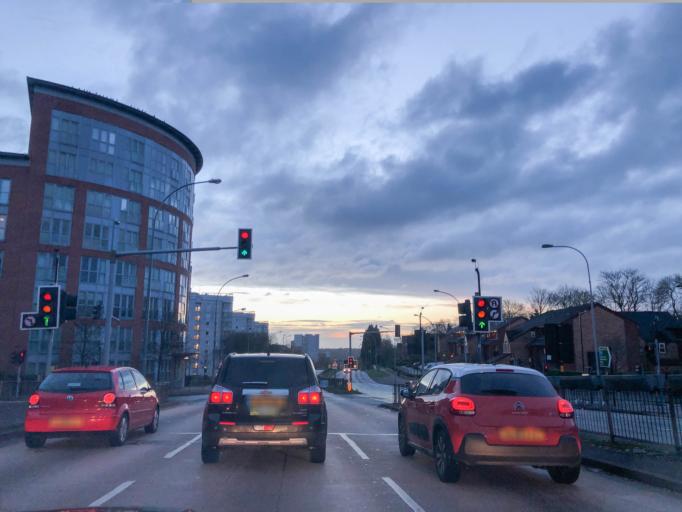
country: GB
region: England
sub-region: City and Borough of Birmingham
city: Birmingham
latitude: 52.4714
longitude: -1.9124
